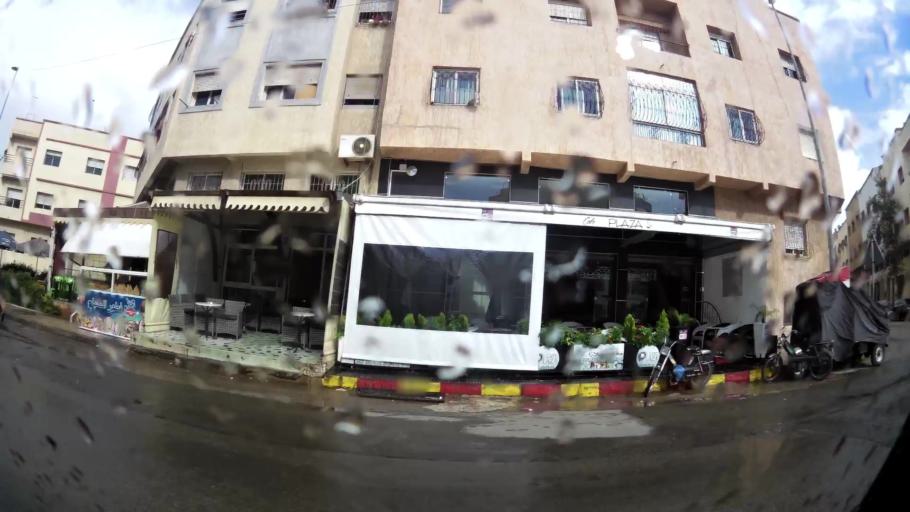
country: MA
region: Grand Casablanca
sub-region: Casablanca
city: Casablanca
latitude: 33.5645
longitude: -7.6938
